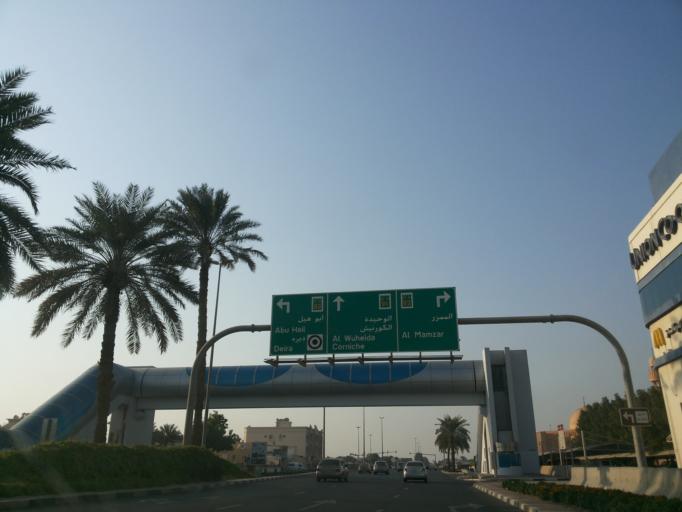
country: AE
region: Ash Shariqah
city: Sharjah
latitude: 25.2824
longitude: 55.3406
